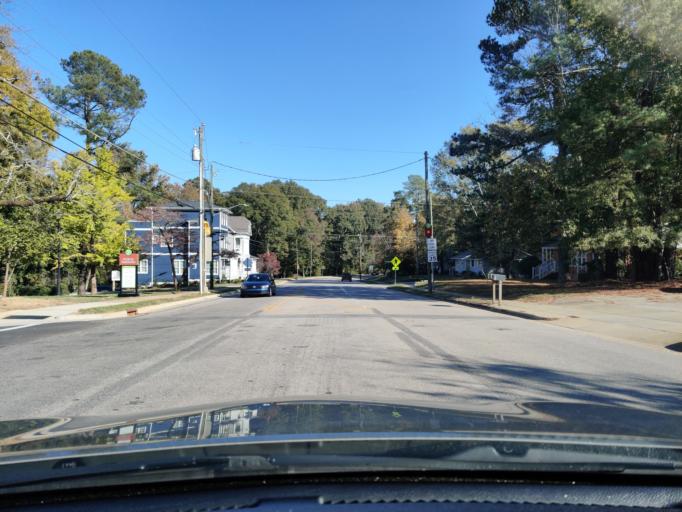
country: US
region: North Carolina
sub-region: Wake County
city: Cary
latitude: 35.7825
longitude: -78.7792
